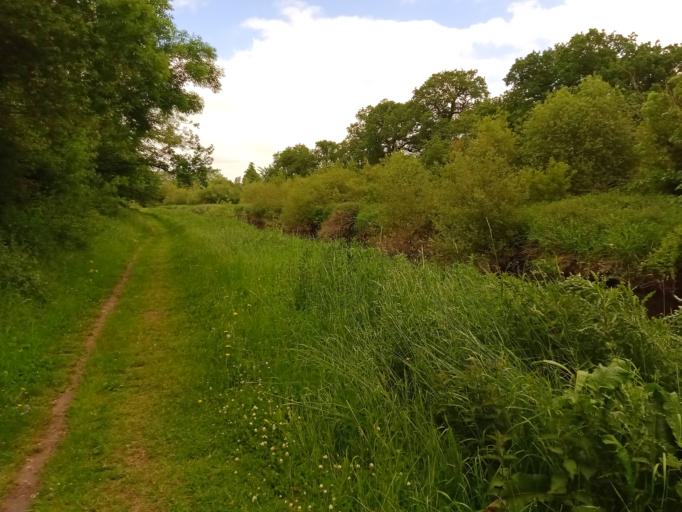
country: IE
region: Leinster
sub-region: County Carlow
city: Carlow
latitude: 52.8146
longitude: -6.9545
